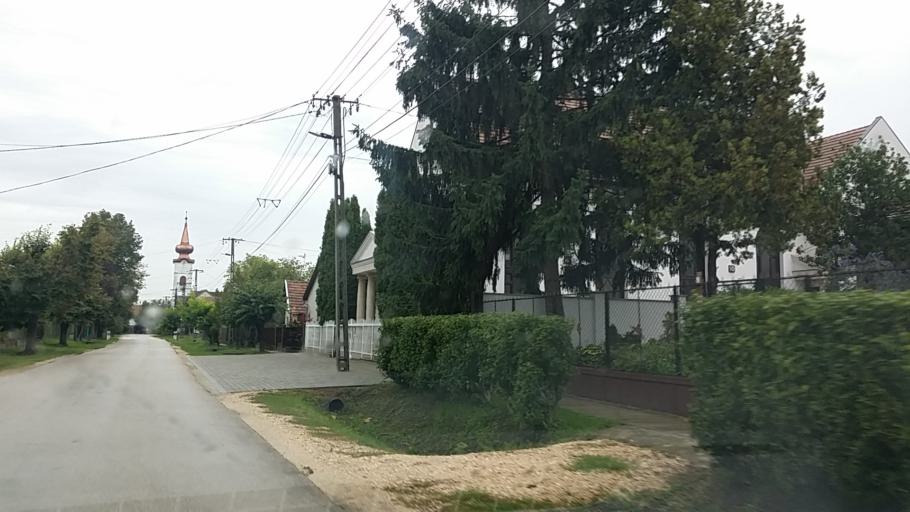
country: HU
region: Pest
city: Domsod
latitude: 47.0906
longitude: 19.0023
